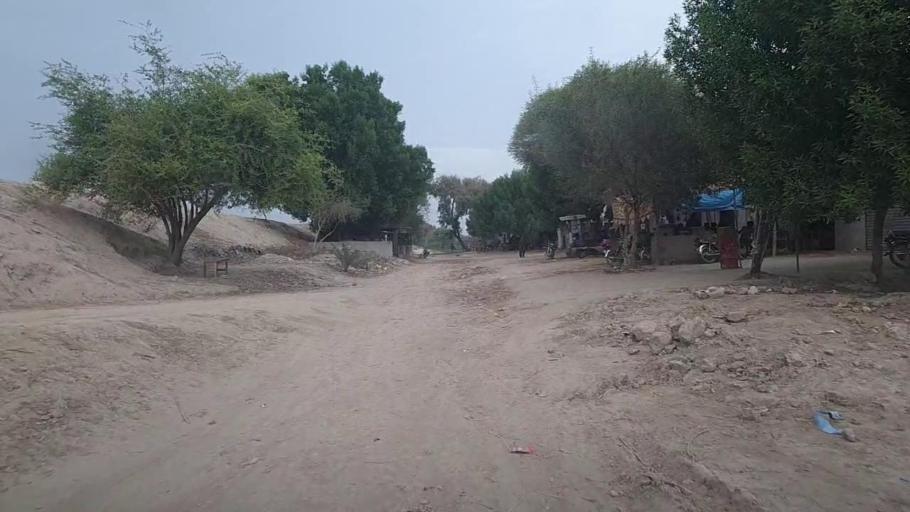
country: PK
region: Sindh
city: Kashmor
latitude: 28.3850
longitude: 69.7951
